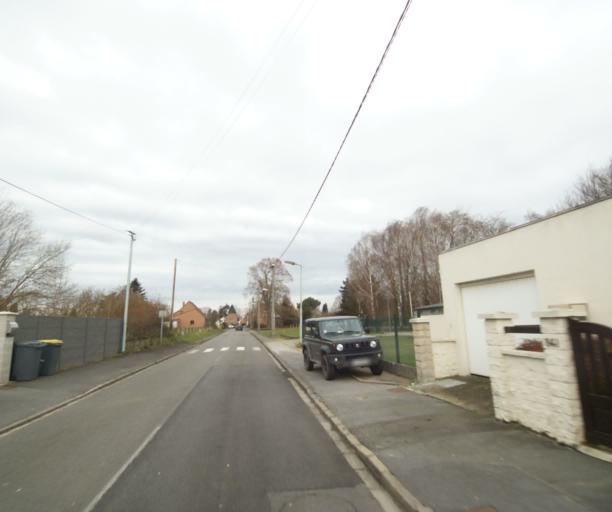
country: FR
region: Nord-Pas-de-Calais
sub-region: Departement du Nord
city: Saint-Saulve
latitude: 50.3622
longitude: 3.5535
